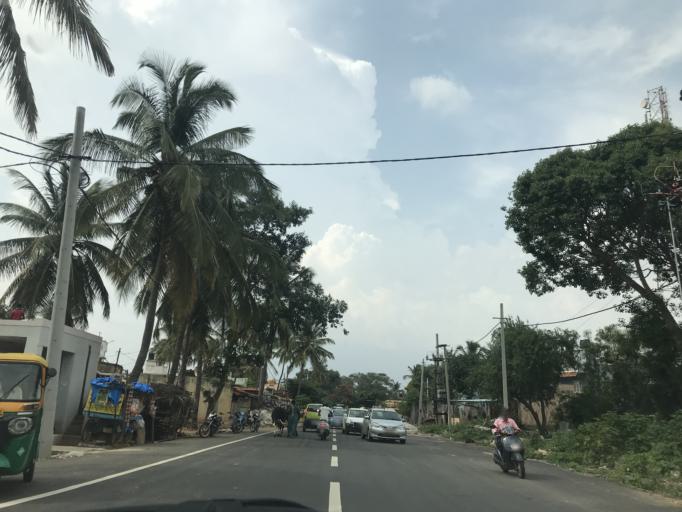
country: IN
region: Karnataka
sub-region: Bangalore Rural
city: Devanhalli
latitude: 13.1711
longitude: 77.6904
